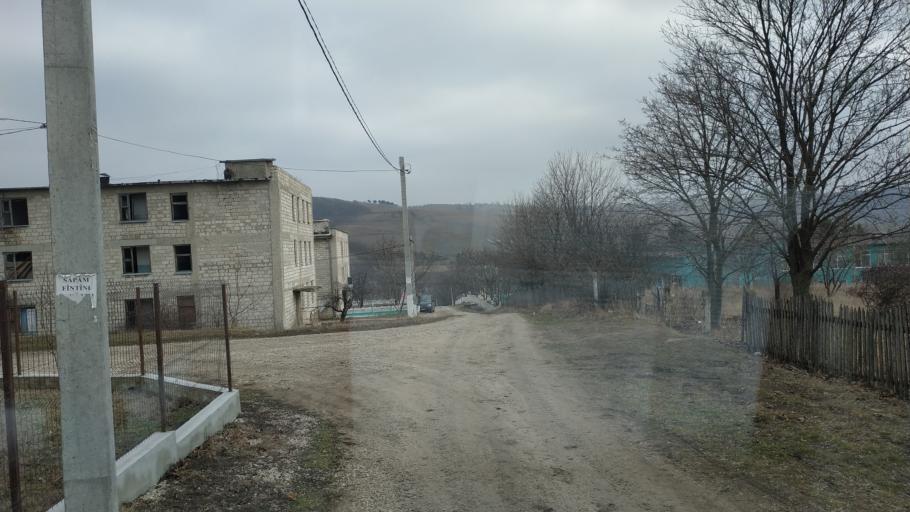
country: MD
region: Hincesti
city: Dancu
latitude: 46.8867
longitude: 28.3205
